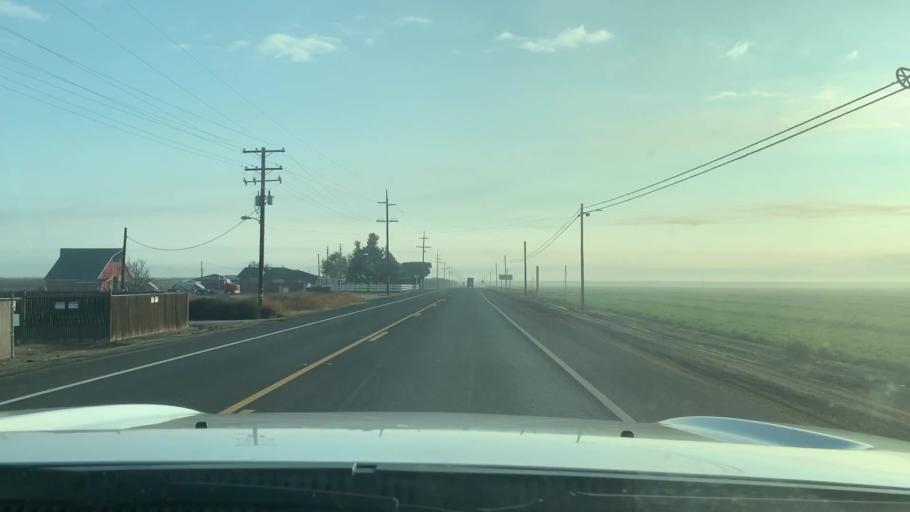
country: US
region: California
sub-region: Kern County
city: Wasco
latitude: 35.6015
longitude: -119.3262
